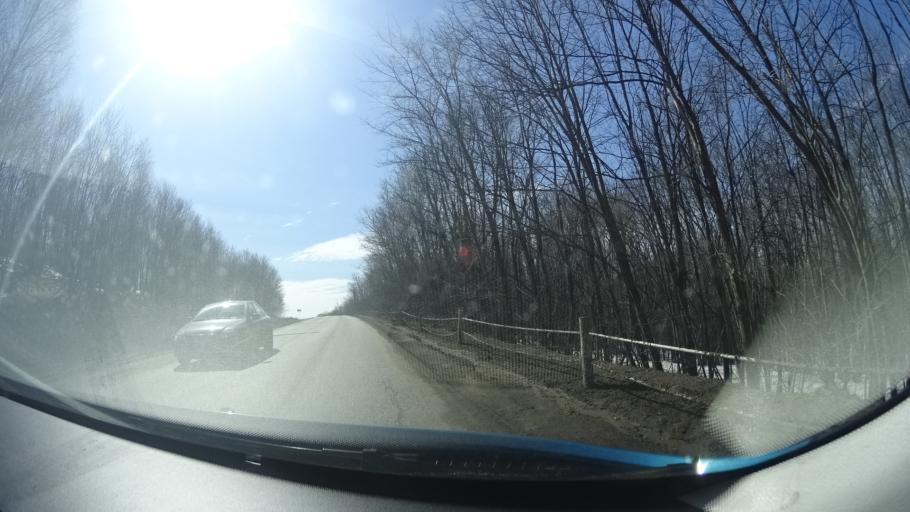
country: RU
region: Bashkortostan
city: Oktyabr'skiy
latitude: 54.4716
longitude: 53.5767
